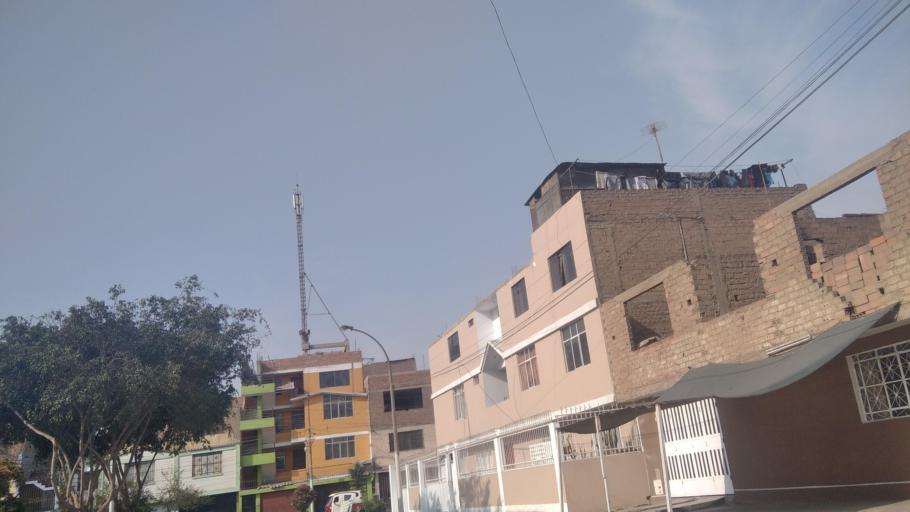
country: PE
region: Lima
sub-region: Lima
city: Independencia
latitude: -11.9855
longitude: -77.0132
